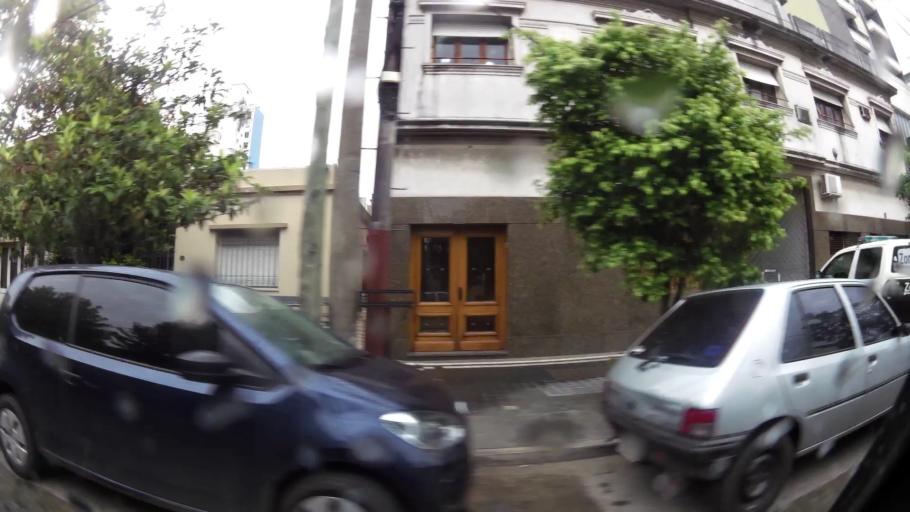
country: AR
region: Buenos Aires
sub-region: Partido de Lanus
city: Lanus
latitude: -34.7006
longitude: -58.3907
